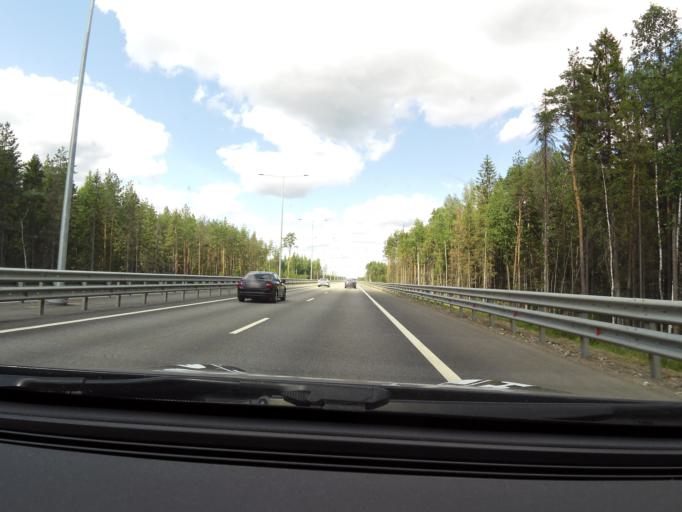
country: RU
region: Tverskaya
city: Krasnomayskiy
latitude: 57.4592
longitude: 34.3887
